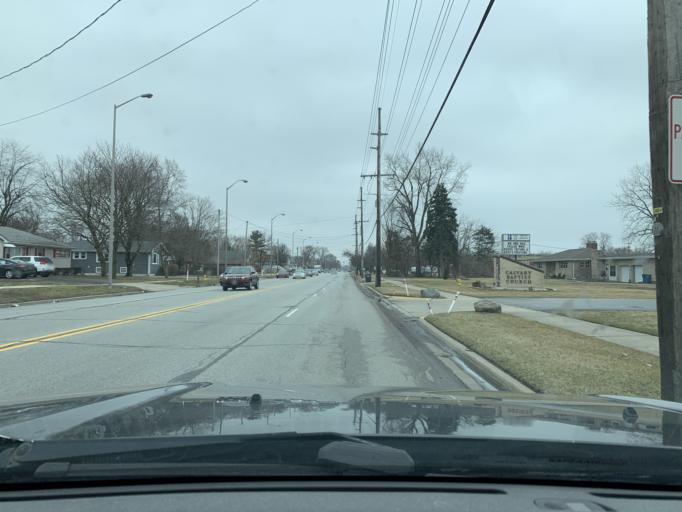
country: US
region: Indiana
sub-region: Lake County
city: Highland
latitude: 41.5408
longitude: -87.4616
